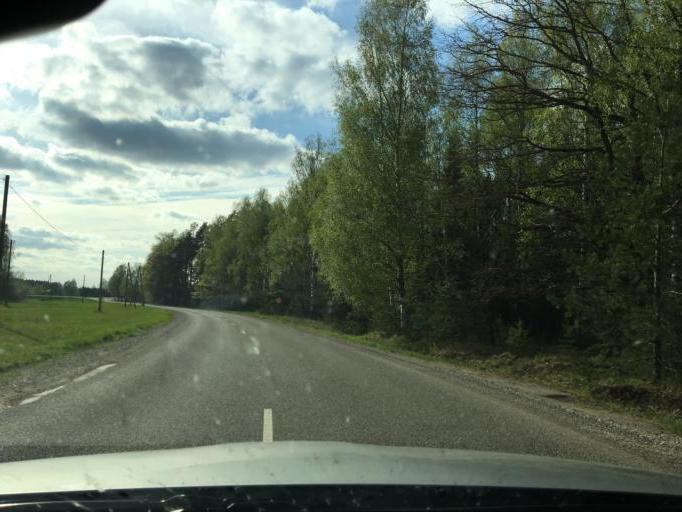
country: LV
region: Ozolnieku
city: Ozolnieki
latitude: 56.6880
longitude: 23.8278
